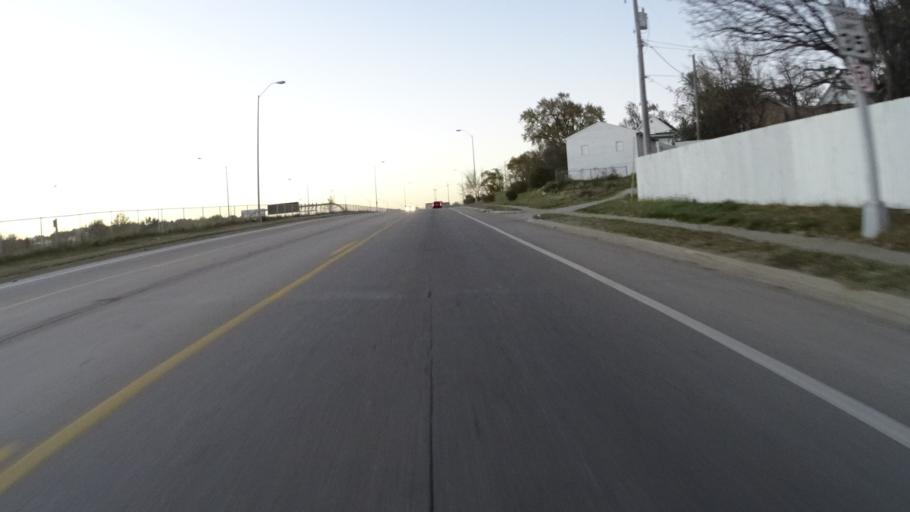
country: US
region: Nebraska
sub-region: Douglas County
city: Omaha
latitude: 41.1993
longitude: -95.9448
